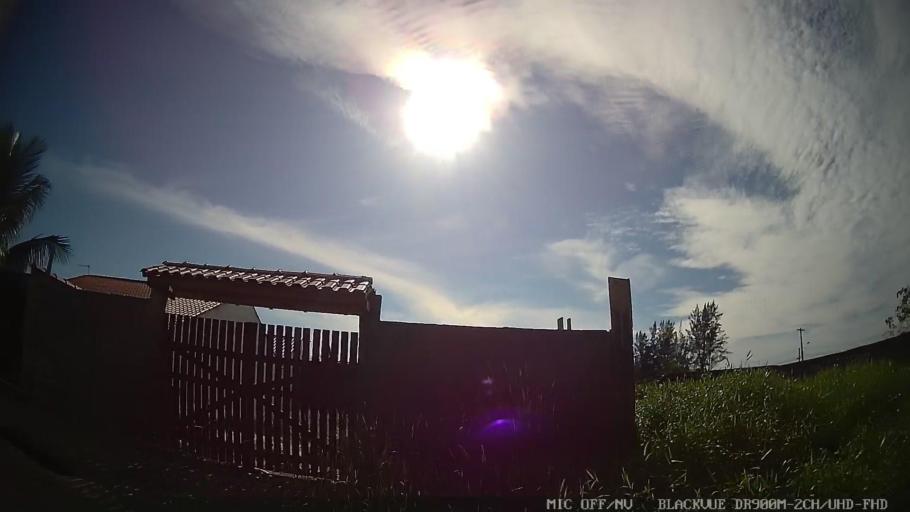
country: BR
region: Sao Paulo
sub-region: Iguape
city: Iguape
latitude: -24.7671
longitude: -47.5818
